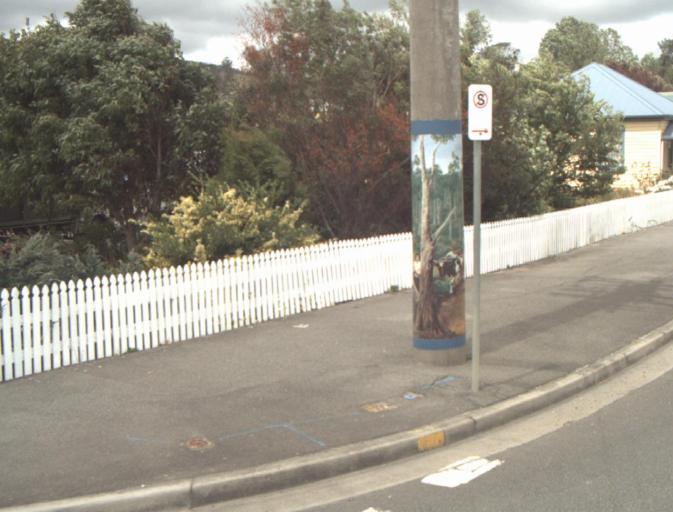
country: AU
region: Tasmania
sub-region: Launceston
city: Mayfield
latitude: -41.2493
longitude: 147.2178
